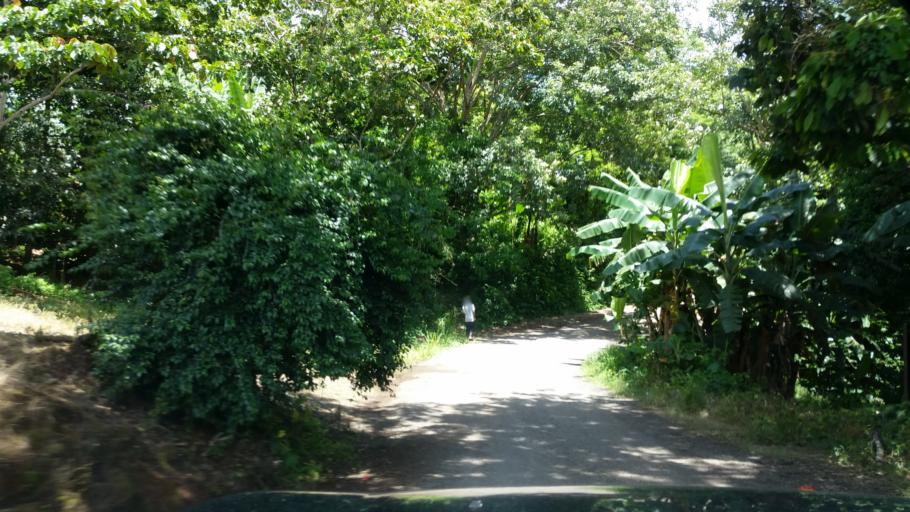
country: NI
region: Atlantico Norte (RAAN)
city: Waslala
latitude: 13.2513
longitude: -85.6144
